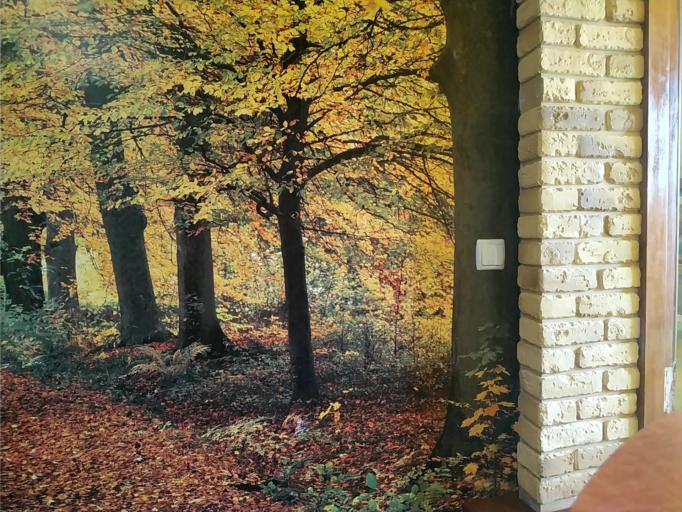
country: RU
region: Vologda
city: Nelazskoye
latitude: 59.4564
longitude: 37.6063
